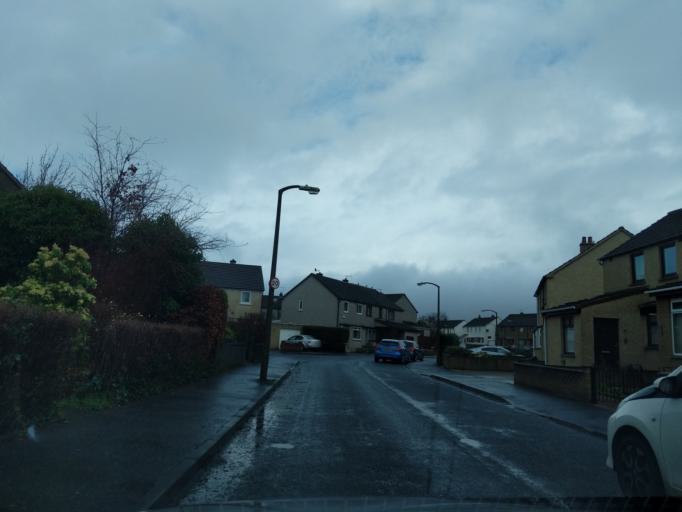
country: GB
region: Scotland
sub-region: Edinburgh
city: Colinton
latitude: 55.9363
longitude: -3.2855
